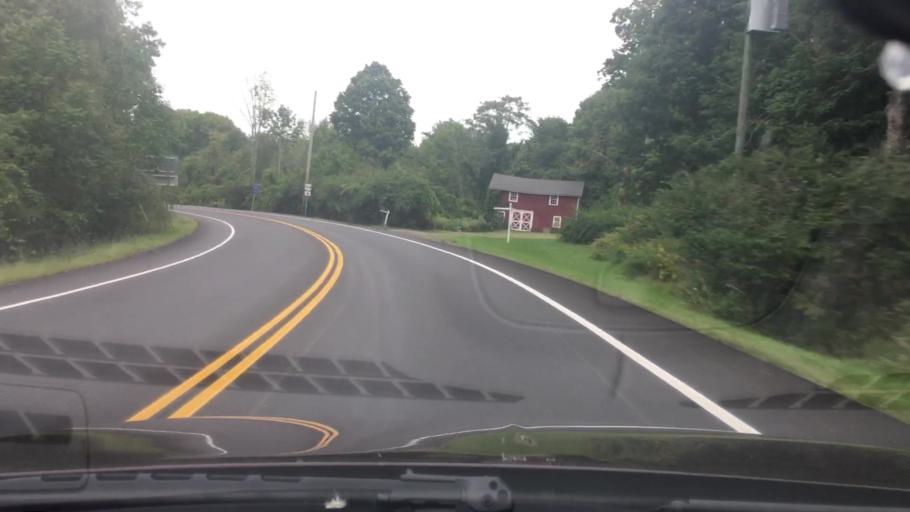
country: US
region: New York
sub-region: Dutchess County
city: Dover Plains
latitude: 41.8458
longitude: -73.5784
